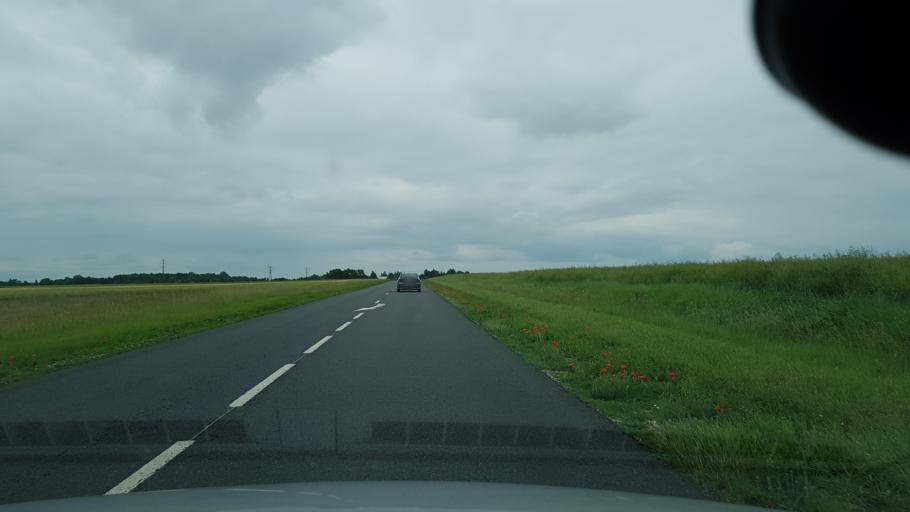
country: FR
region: Centre
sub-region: Departement du Loir-et-Cher
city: Chatillon-sur-Cher
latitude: 47.2989
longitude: 1.5157
